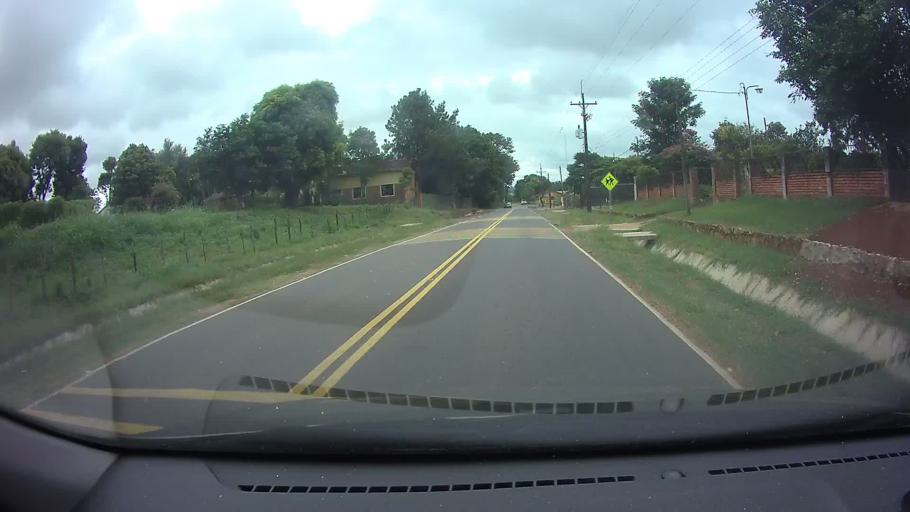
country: PY
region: Central
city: Nueva Italia
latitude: -25.6052
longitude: -57.4152
